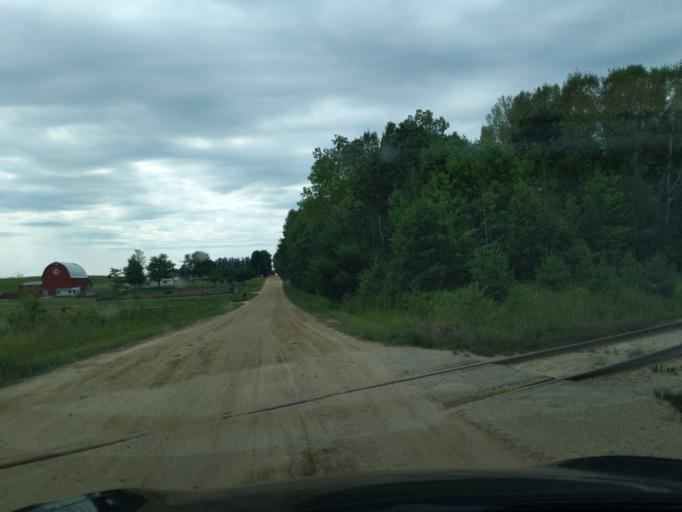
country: US
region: Michigan
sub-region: Clare County
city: Harrison
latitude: 44.0025
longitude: -84.9742
